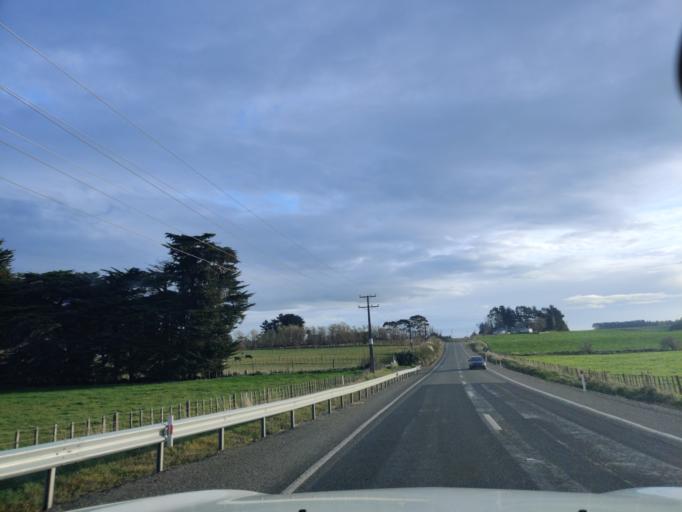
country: NZ
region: Manawatu-Wanganui
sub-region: Palmerston North City
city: Palmerston North
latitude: -40.4033
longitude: 175.6190
